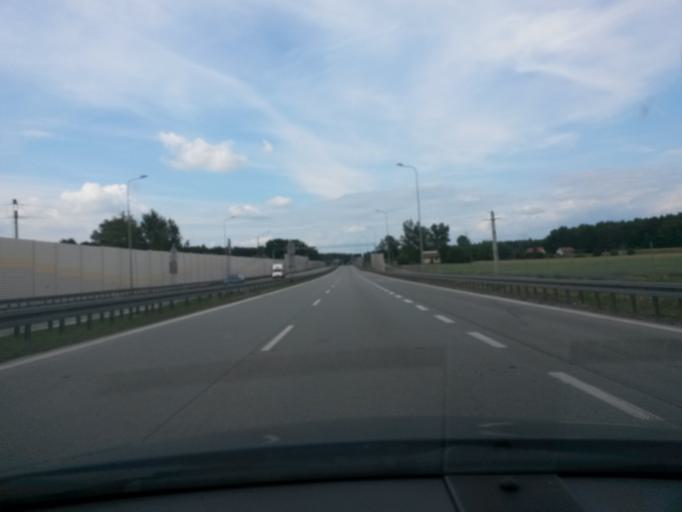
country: PL
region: Lodz Voivodeship
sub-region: Powiat skierniewicki
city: Kowiesy
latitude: 51.9191
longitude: 20.4557
